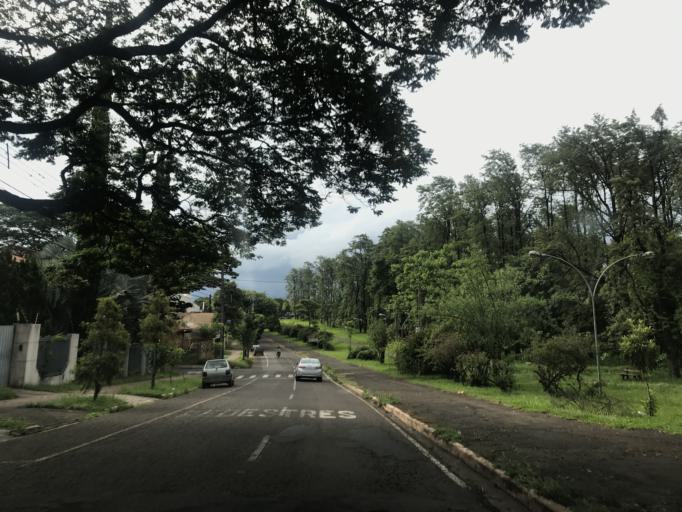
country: BR
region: Parana
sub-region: Maringa
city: Maringa
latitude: -23.4282
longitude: -51.9620
